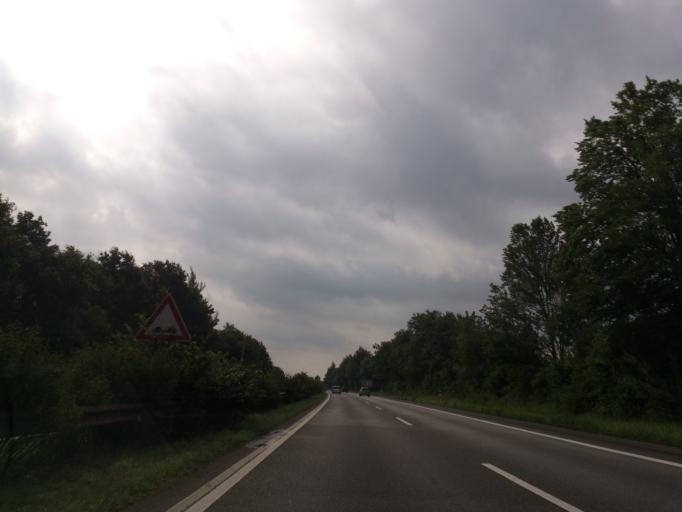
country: DE
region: Schleswig-Holstein
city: Seeth-Ekholt
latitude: 53.7337
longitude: 9.7208
